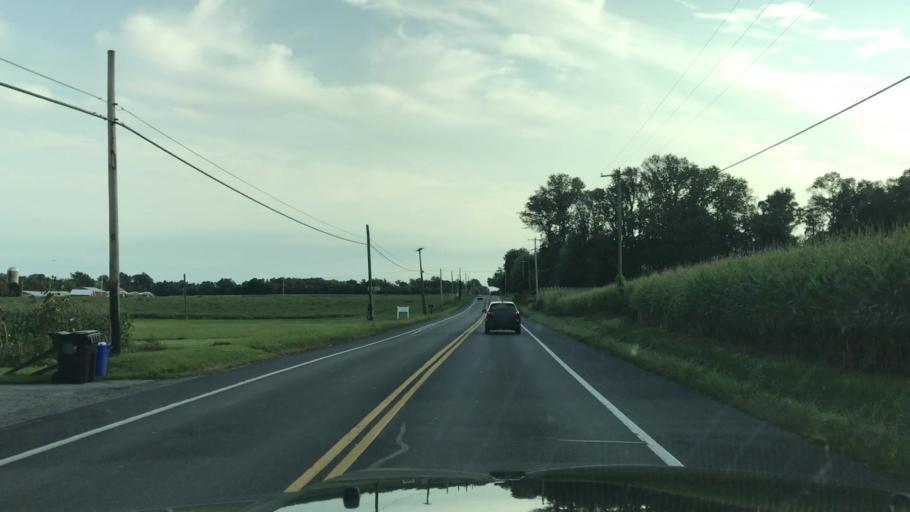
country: US
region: Pennsylvania
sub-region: Berks County
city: Bally
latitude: 40.4147
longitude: -75.5763
